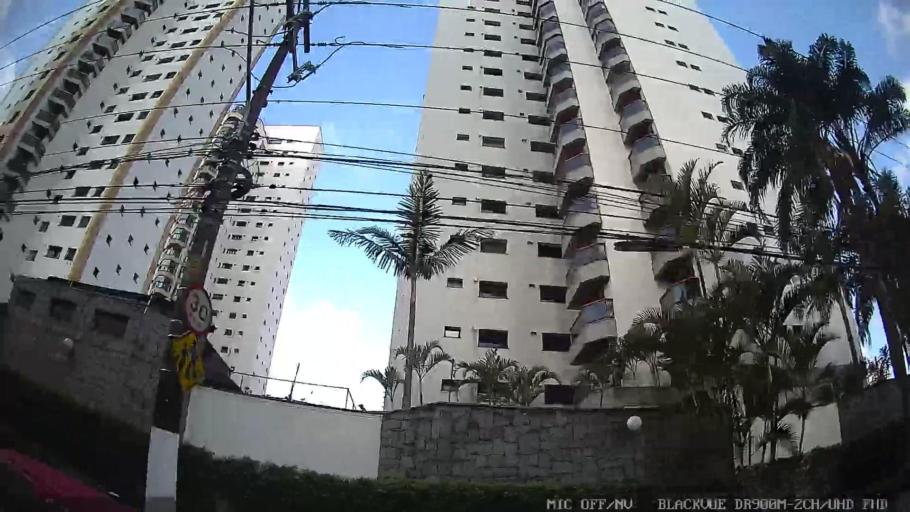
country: BR
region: Sao Paulo
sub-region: Sao Caetano Do Sul
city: Sao Caetano do Sul
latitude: -23.5511
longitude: -46.5570
